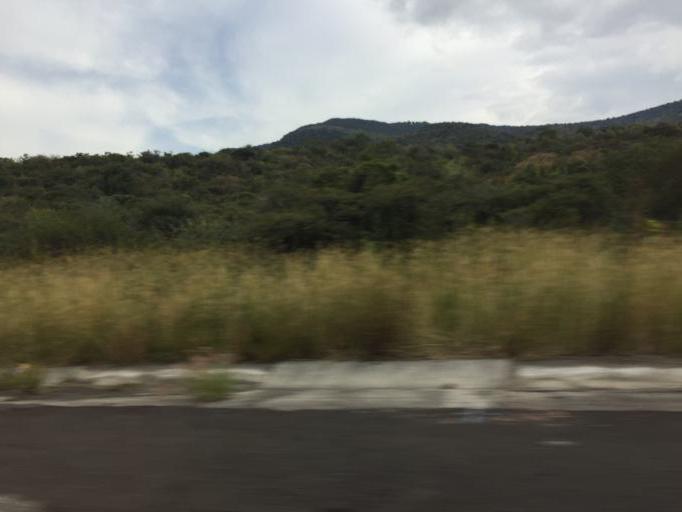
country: MX
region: Mexico
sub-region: Chapultepec
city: Chucandiro
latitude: 19.8867
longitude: -101.3290
